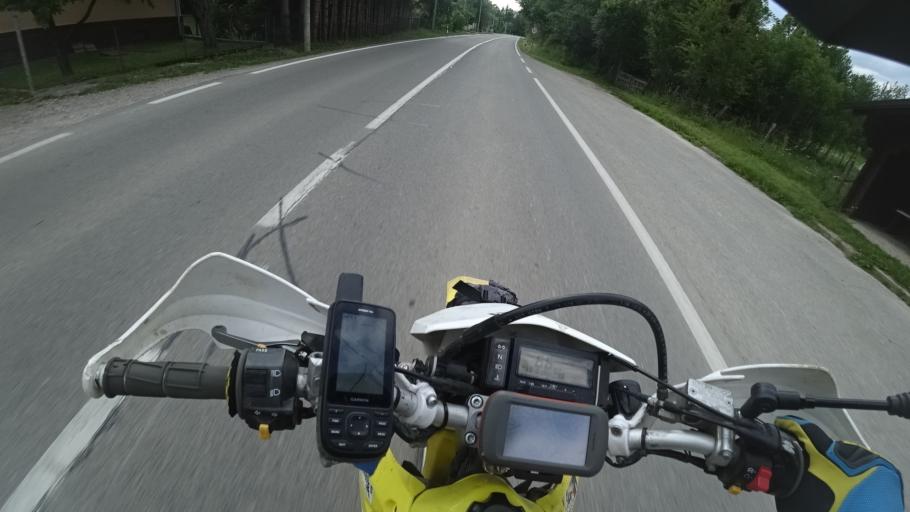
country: HR
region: Licko-Senjska
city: Gospic
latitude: 44.5155
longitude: 15.4208
